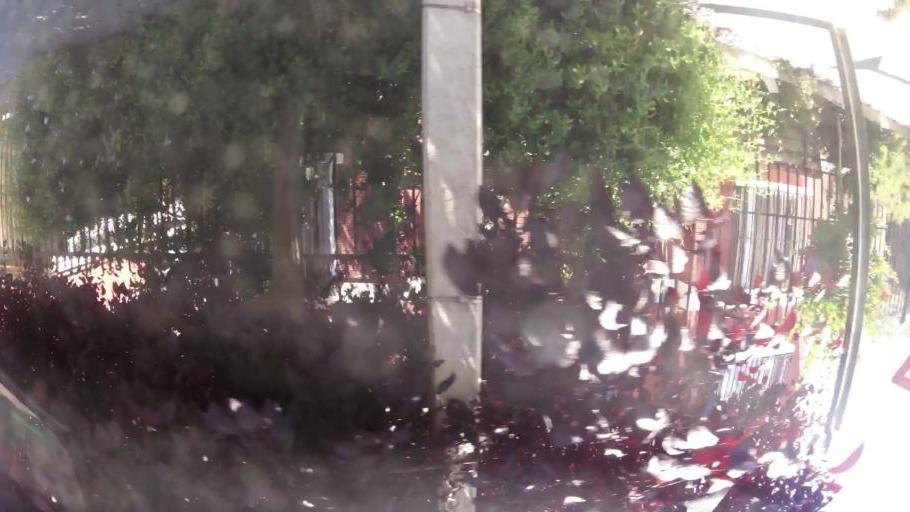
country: CL
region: Santiago Metropolitan
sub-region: Provincia de Maipo
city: San Bernardo
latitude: -33.6249
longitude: -70.7106
